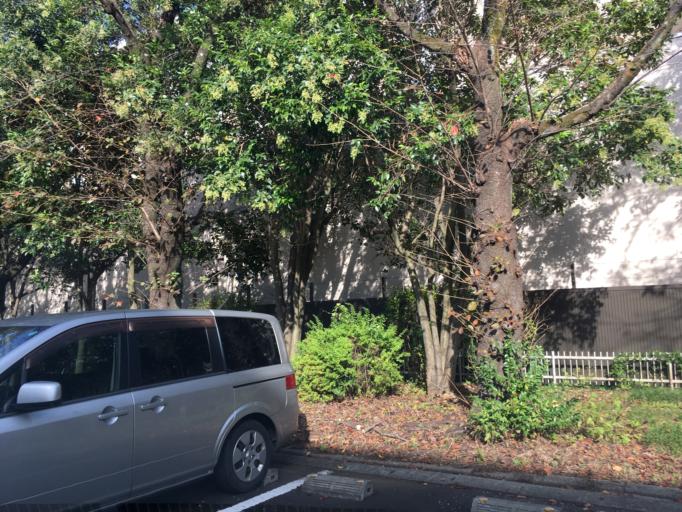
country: JP
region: Saitama
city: Tokorozawa
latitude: 35.8000
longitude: 139.4713
